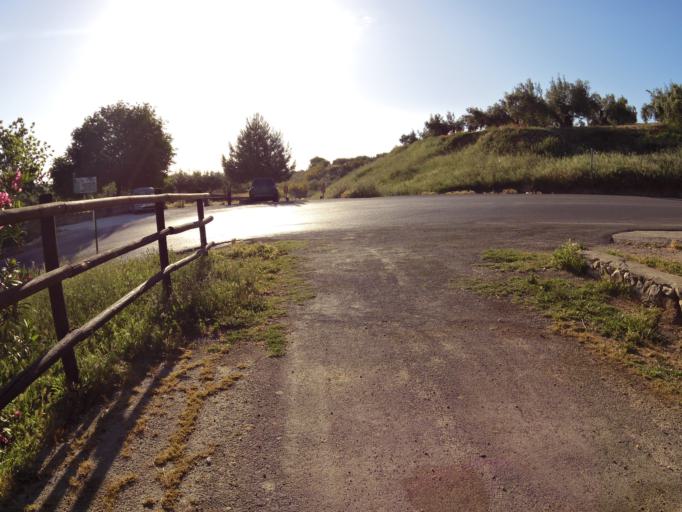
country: ES
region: Andalusia
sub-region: Province of Cordoba
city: Luque
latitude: 37.5707
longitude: -4.2806
